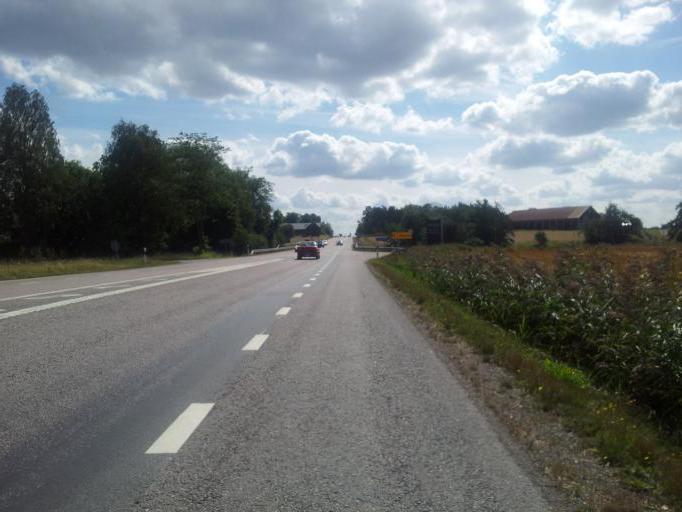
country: SE
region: Uppsala
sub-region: Uppsala Kommun
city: Gamla Uppsala
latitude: 59.9104
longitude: 17.6074
